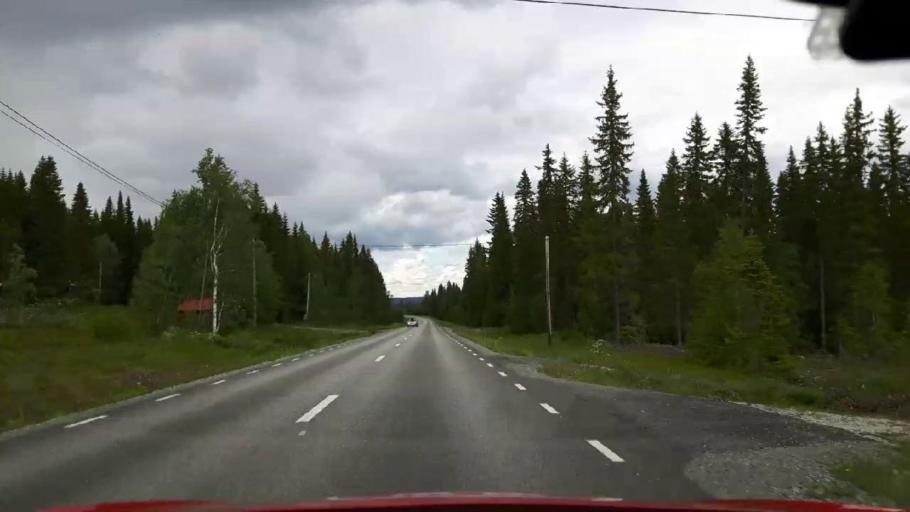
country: SE
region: Jaemtland
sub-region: Krokoms Kommun
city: Krokom
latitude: 63.6959
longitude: 14.3194
